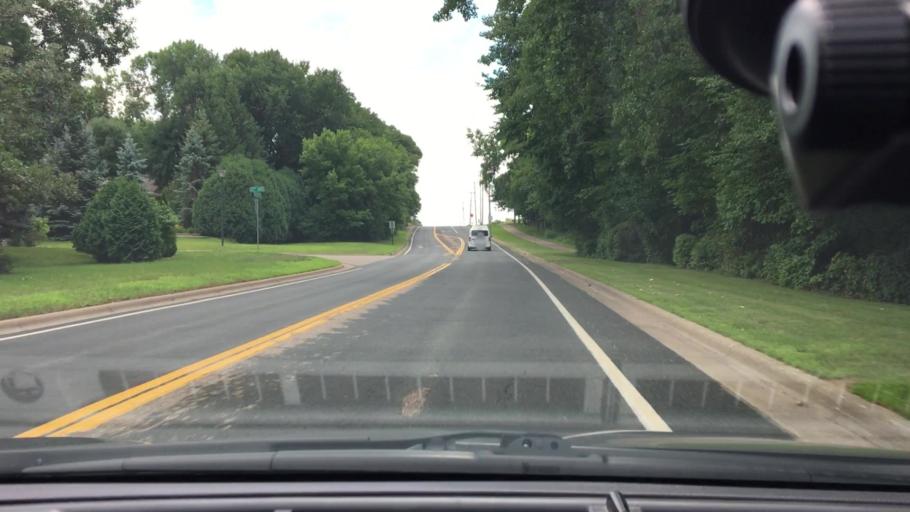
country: US
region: Minnesota
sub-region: Hennepin County
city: New Hope
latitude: 45.0238
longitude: -93.4209
